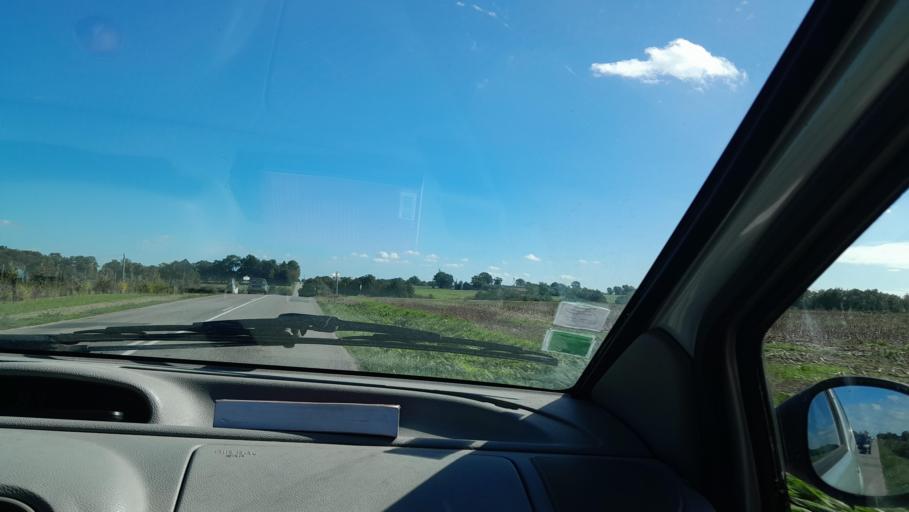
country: FR
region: Pays de la Loire
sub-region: Departement de la Mayenne
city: Cosse-le-Vivien
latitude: 47.9386
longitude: -0.8678
